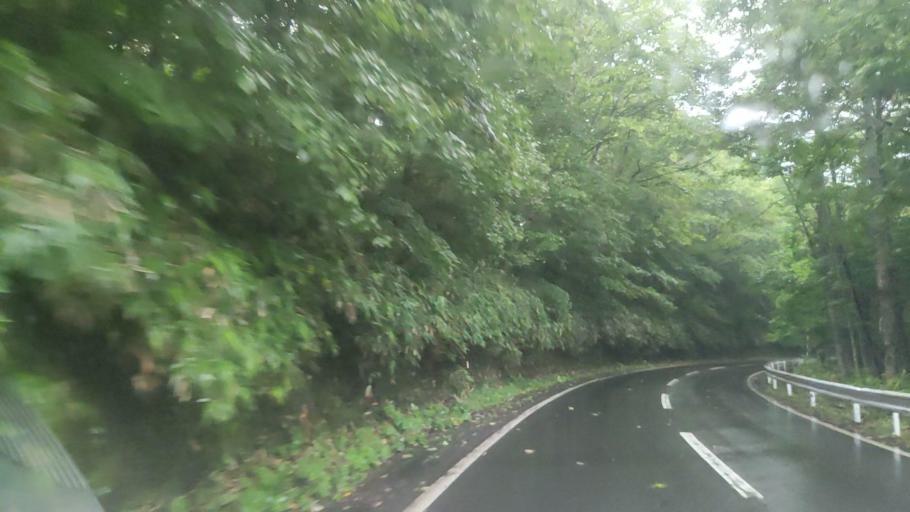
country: JP
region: Hokkaido
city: Muroran
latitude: 42.5219
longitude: 141.1116
